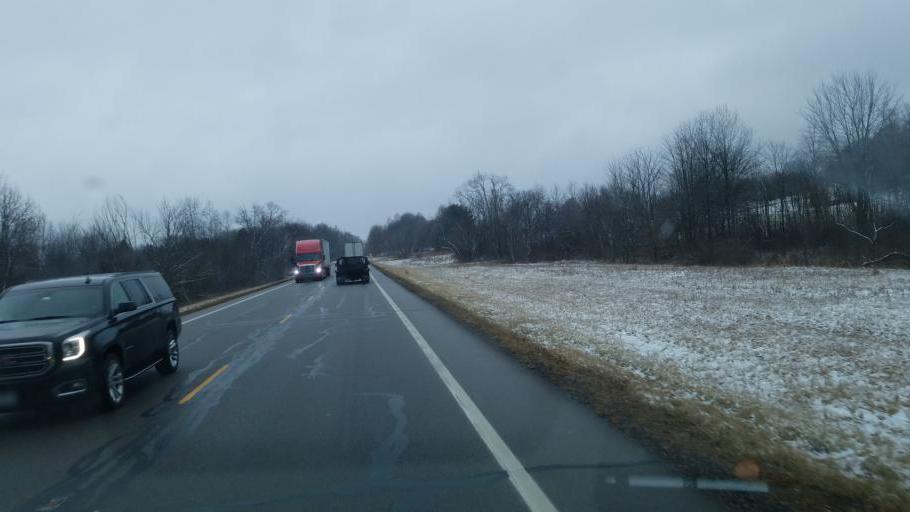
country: US
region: Ohio
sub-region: Wayne County
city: Doylestown
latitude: 40.9734
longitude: -81.7062
